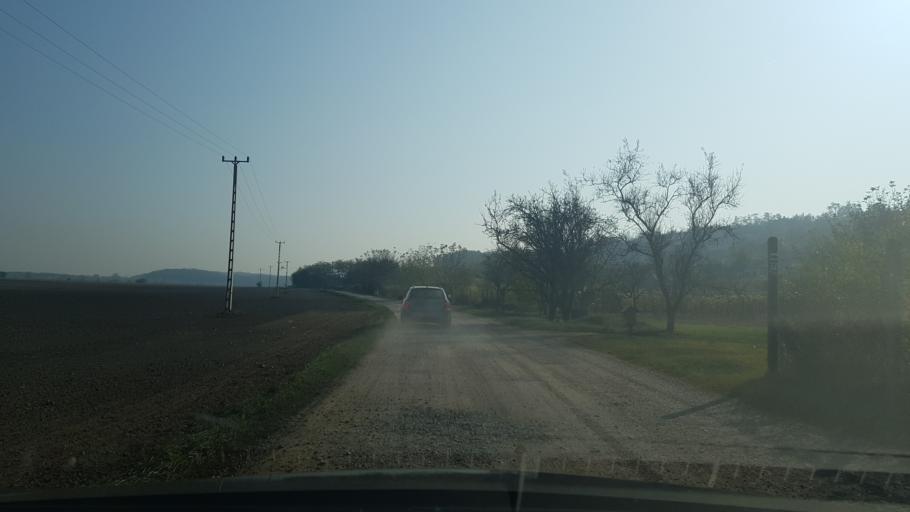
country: HU
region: Fejer
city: Adony
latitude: 47.0829
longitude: 18.8513
